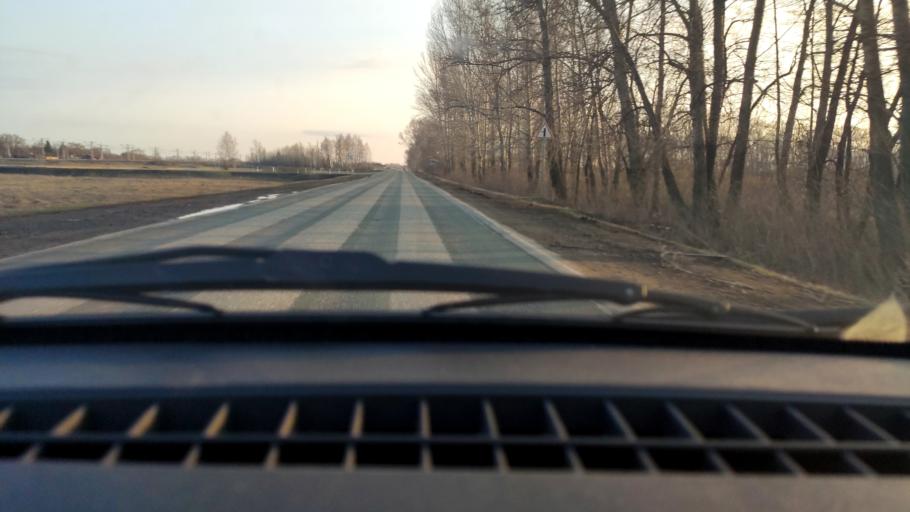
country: RU
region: Bashkortostan
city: Chishmy
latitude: 54.4519
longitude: 55.2488
